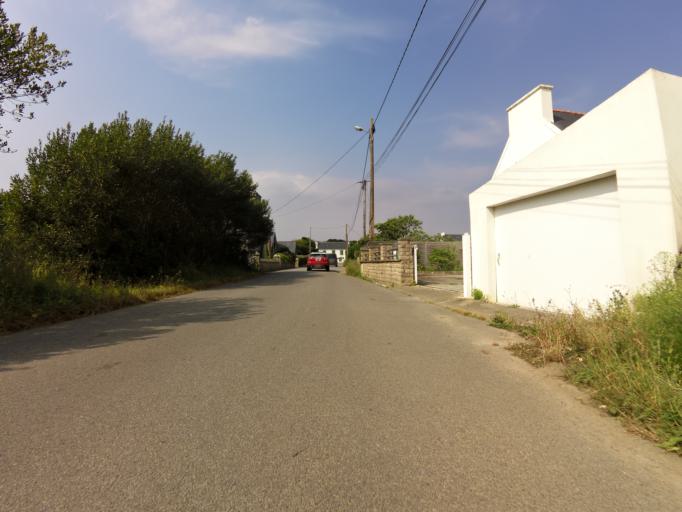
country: FR
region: Brittany
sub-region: Departement du Finistere
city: Esquibien
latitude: 48.0155
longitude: -4.5651
